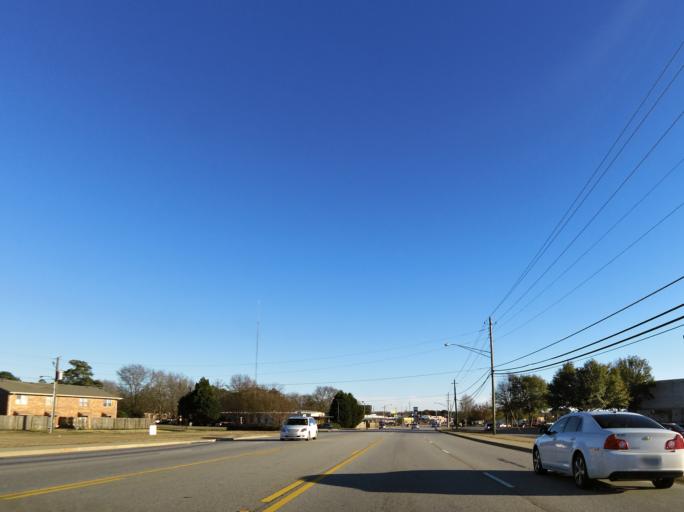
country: US
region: Georgia
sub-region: Houston County
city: Centerville
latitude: 32.6221
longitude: -83.6855
